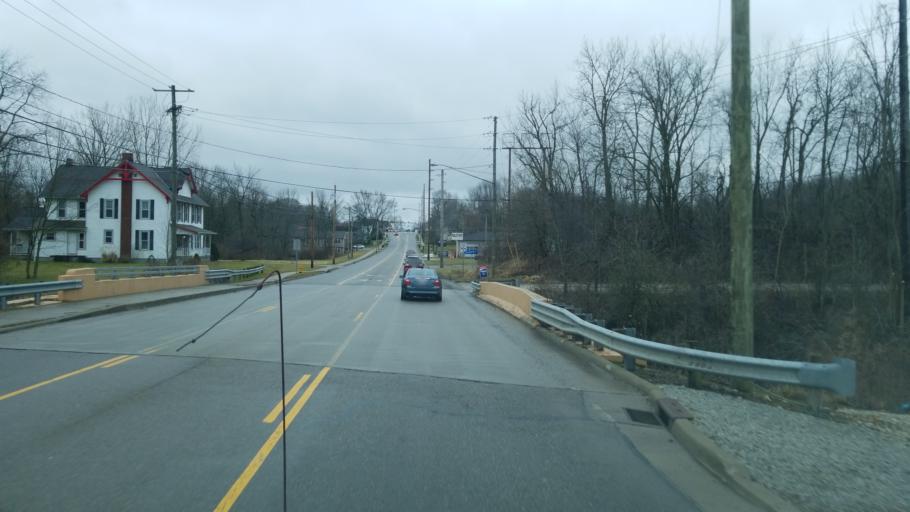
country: US
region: Ohio
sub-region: Summit County
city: Norton
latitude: 41.0101
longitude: -81.6386
